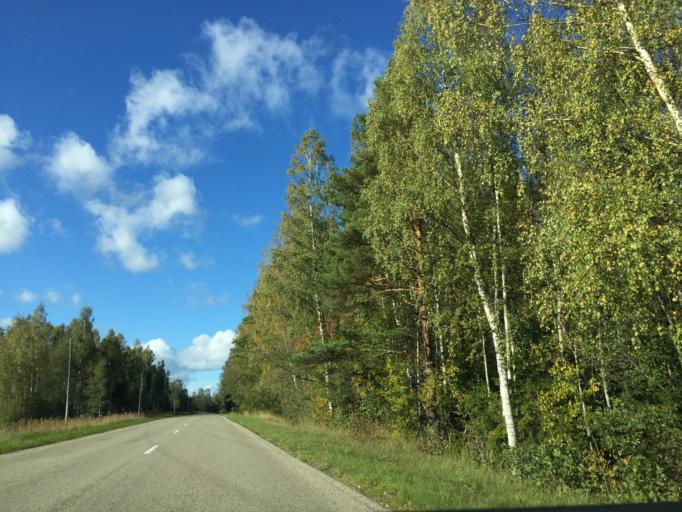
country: LV
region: Rojas
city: Roja
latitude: 57.4236
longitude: 22.9223
